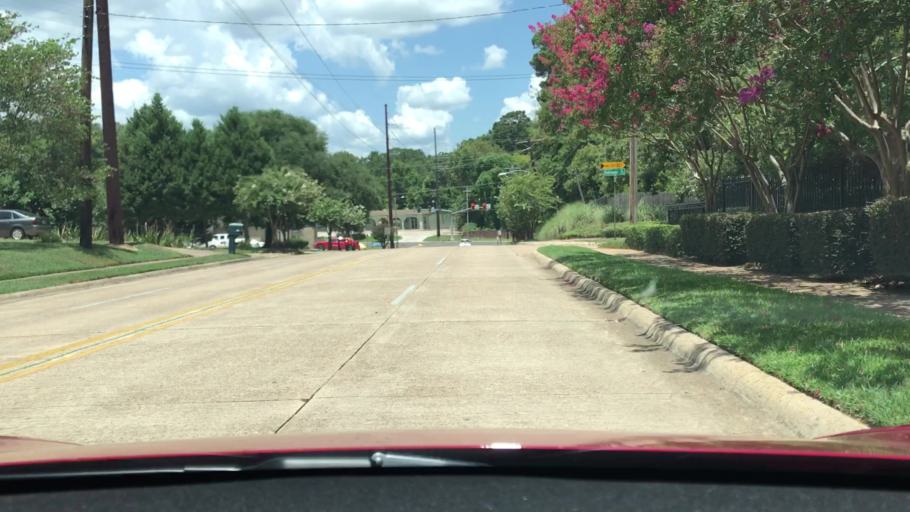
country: US
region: Louisiana
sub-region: Bossier Parish
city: Bossier City
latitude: 32.4416
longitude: -93.7377
